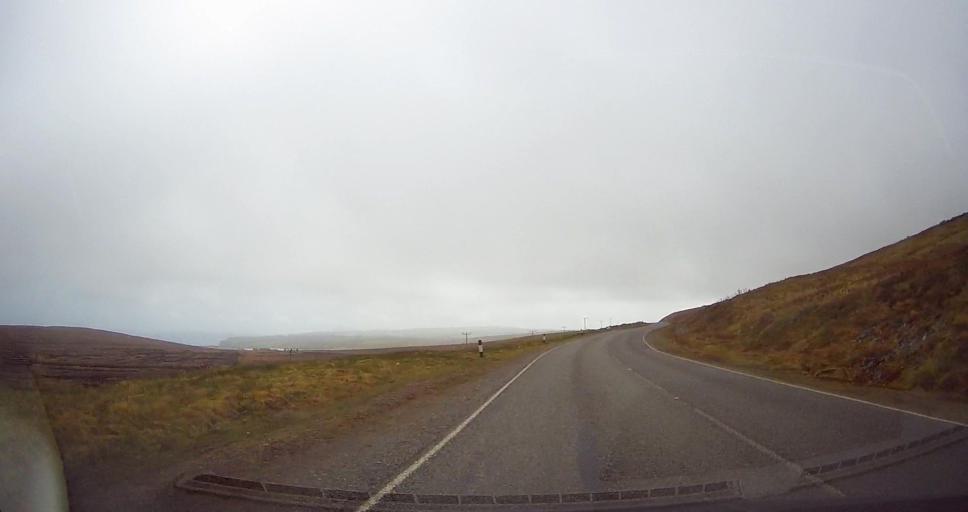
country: GB
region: Scotland
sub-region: Shetland Islands
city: Sandwick
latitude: 59.9604
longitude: -1.2839
